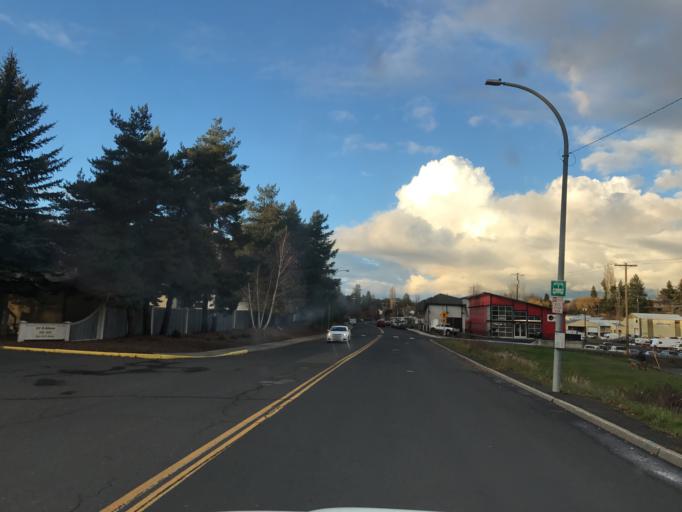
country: US
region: Idaho
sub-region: Latah County
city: Moscow
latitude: 46.7379
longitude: -117.0041
